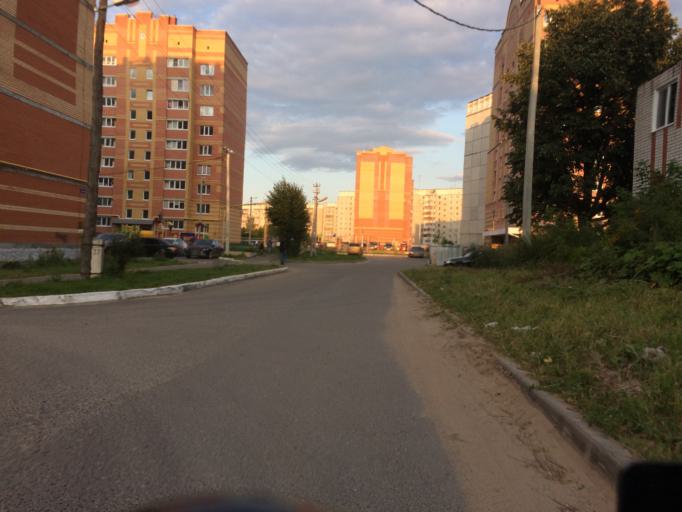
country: RU
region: Mariy-El
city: Medvedevo
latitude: 56.6442
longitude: 47.8464
